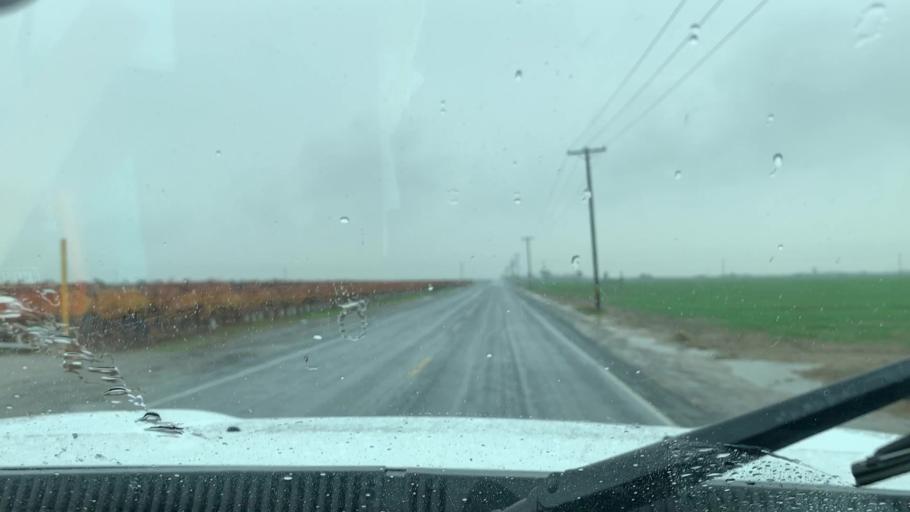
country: US
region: California
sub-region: Tulare County
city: Earlimart
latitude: 35.8919
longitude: -119.2992
